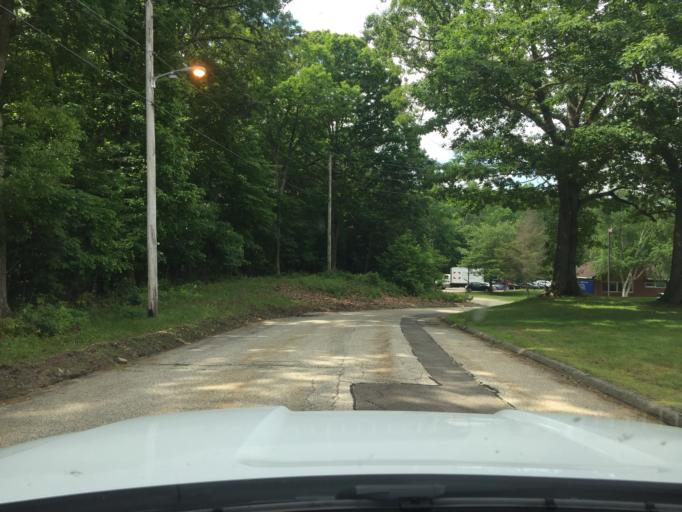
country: US
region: Connecticut
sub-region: Tolland County
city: South Coventry
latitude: 41.8058
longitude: -72.2921
